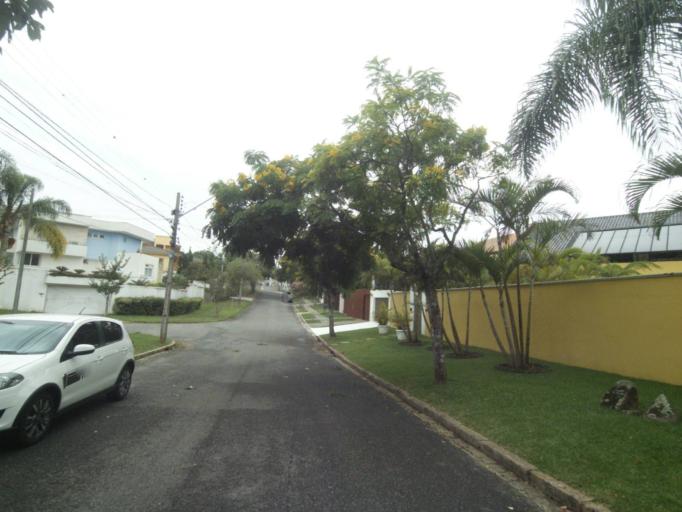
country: BR
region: Parana
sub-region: Curitiba
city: Curitiba
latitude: -25.4050
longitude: -49.2836
